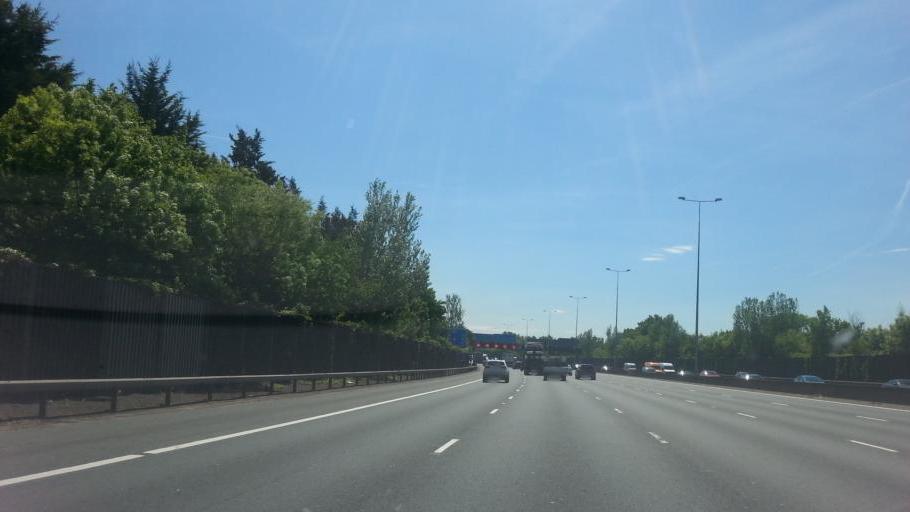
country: GB
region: England
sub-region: Surrey
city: Egham
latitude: 51.4287
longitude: -0.5406
